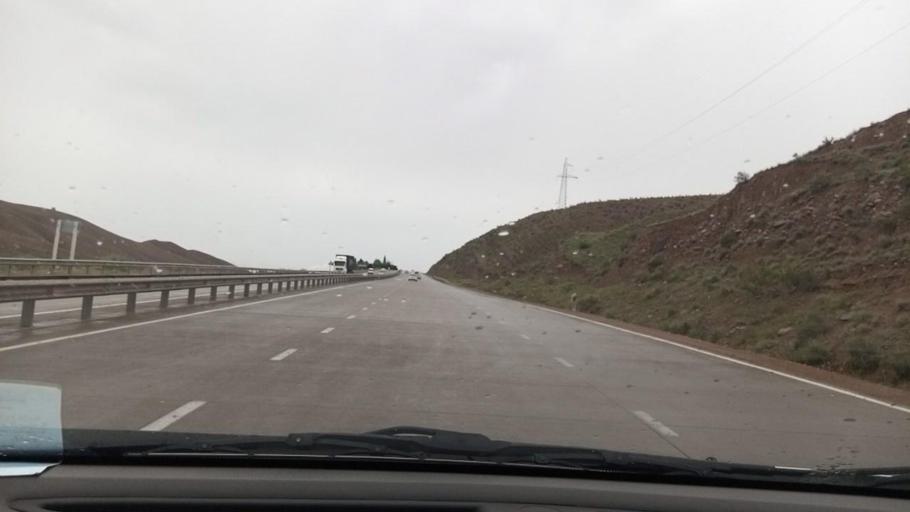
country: UZ
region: Namangan
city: Pop Shahri
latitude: 40.9457
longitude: 70.6834
